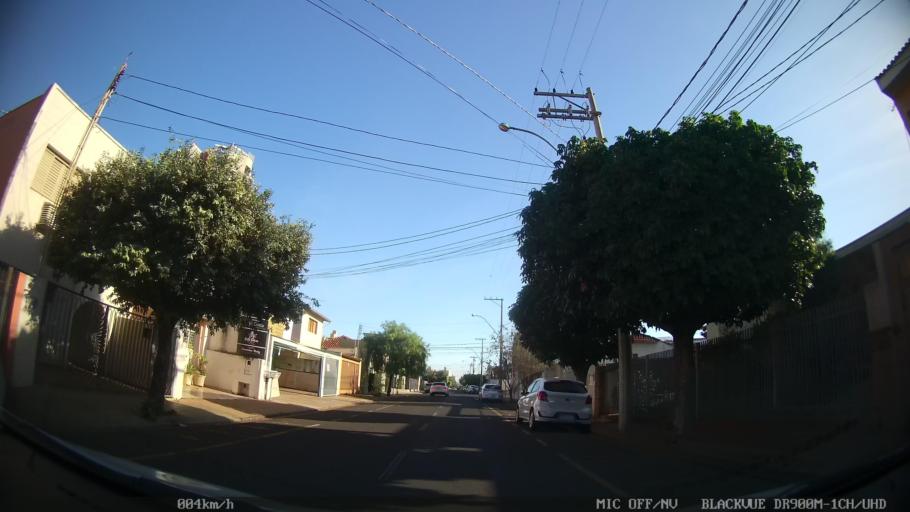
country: BR
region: Sao Paulo
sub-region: Sao Jose Do Rio Preto
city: Sao Jose do Rio Preto
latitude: -20.8081
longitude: -49.3866
